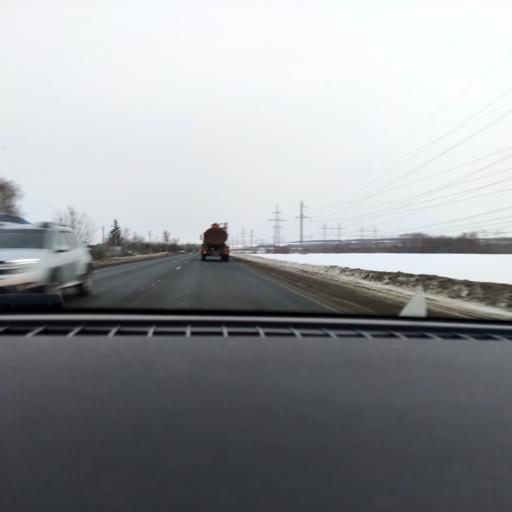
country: RU
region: Samara
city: Smyshlyayevka
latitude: 53.0942
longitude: 50.3997
